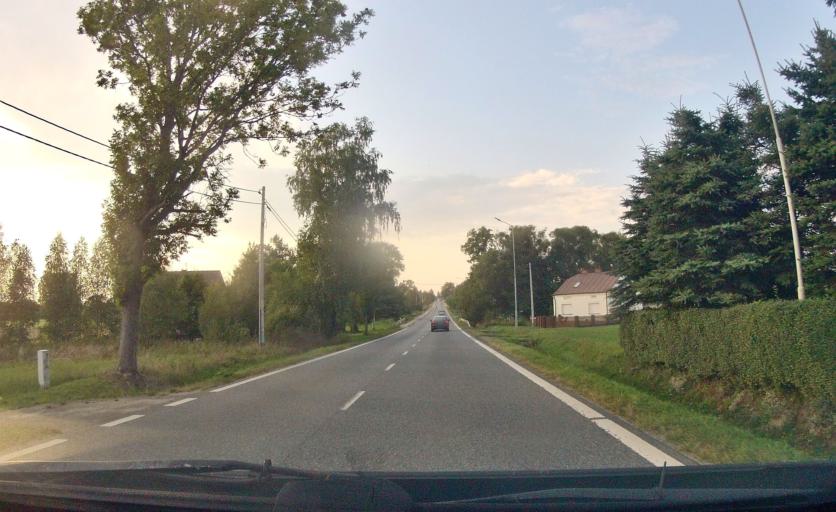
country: PL
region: Subcarpathian Voivodeship
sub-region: Powiat jasielski
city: Nowy Zmigrod
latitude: 49.5970
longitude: 21.5330
